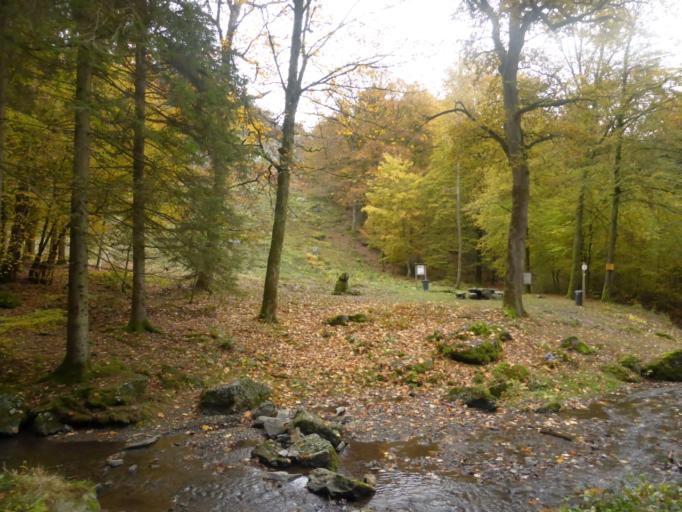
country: BE
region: Wallonia
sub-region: Province du Luxembourg
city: Herbeumont
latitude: 49.7347
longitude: 5.1826
